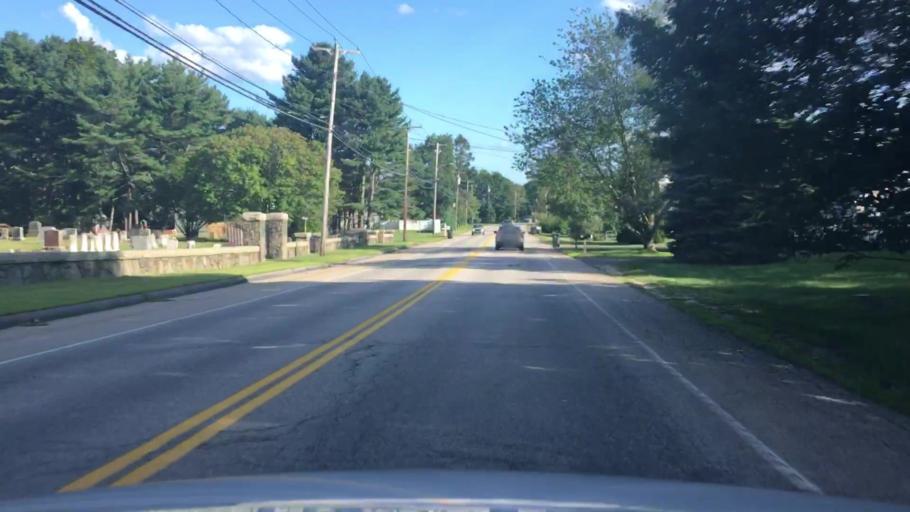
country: US
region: Maine
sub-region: Cumberland County
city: Scarborough
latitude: 43.5717
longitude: -70.3172
